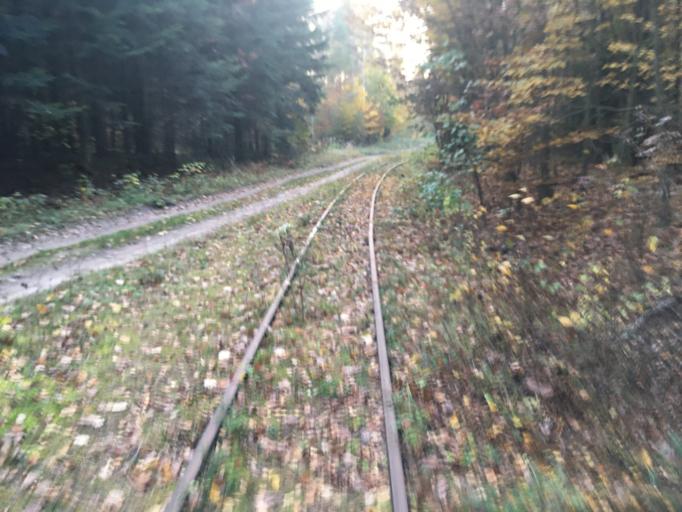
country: PL
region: Swietokrzyskie
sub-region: Powiat starachowicki
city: Starachowice
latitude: 51.0662
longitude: 21.1341
